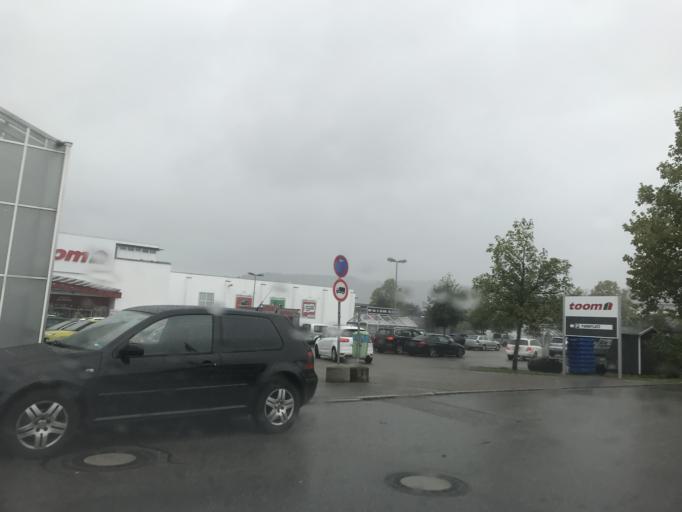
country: DE
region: Baden-Wuerttemberg
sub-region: Freiburg Region
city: Schopfheim
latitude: 47.6421
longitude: 7.8115
